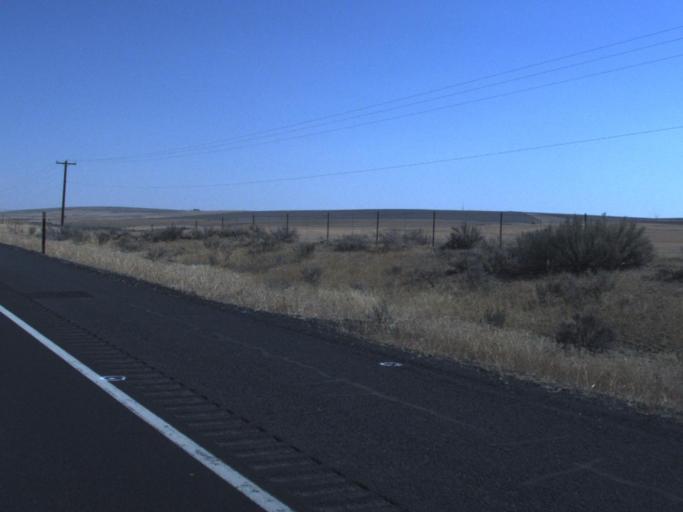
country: US
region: Washington
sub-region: Grant County
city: Warden
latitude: 47.0841
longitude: -118.9571
